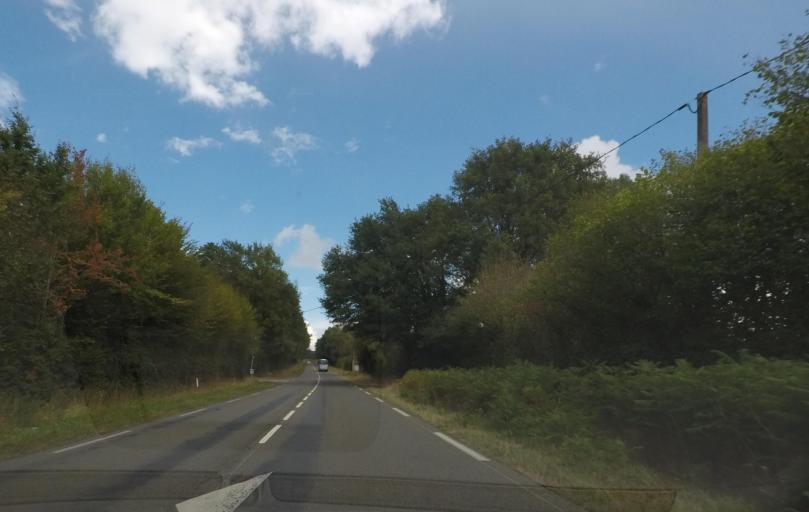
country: FR
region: Pays de la Loire
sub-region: Departement de la Sarthe
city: Beaufay
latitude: 48.1441
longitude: 0.3829
